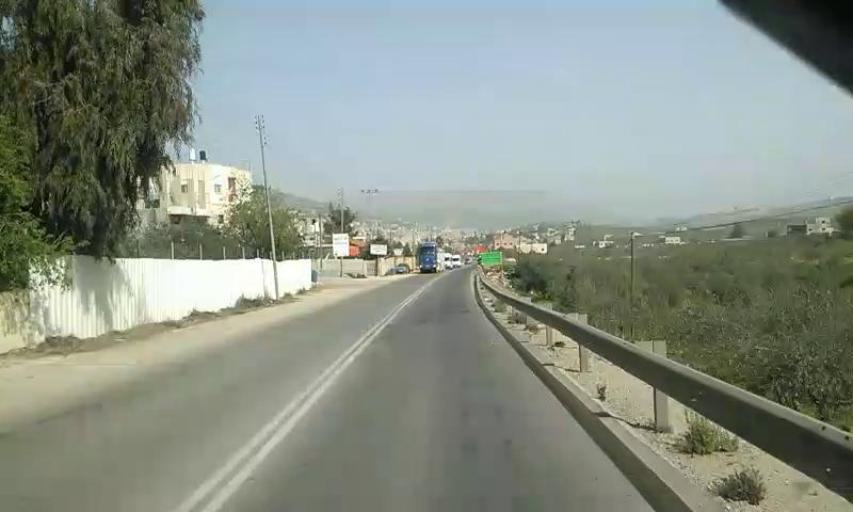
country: PS
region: West Bank
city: `Aynabus
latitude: 32.1326
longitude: 35.2577
